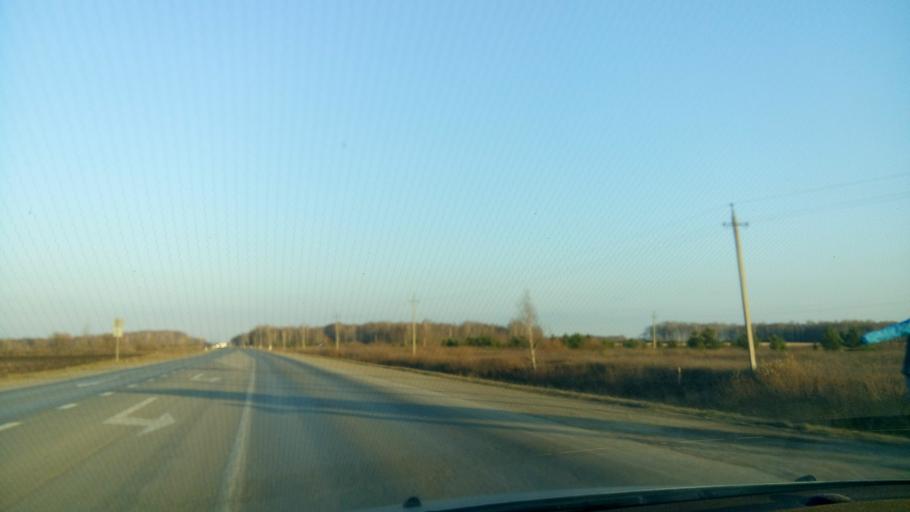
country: RU
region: Sverdlovsk
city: Bogdanovich
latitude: 56.7537
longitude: 62.1064
